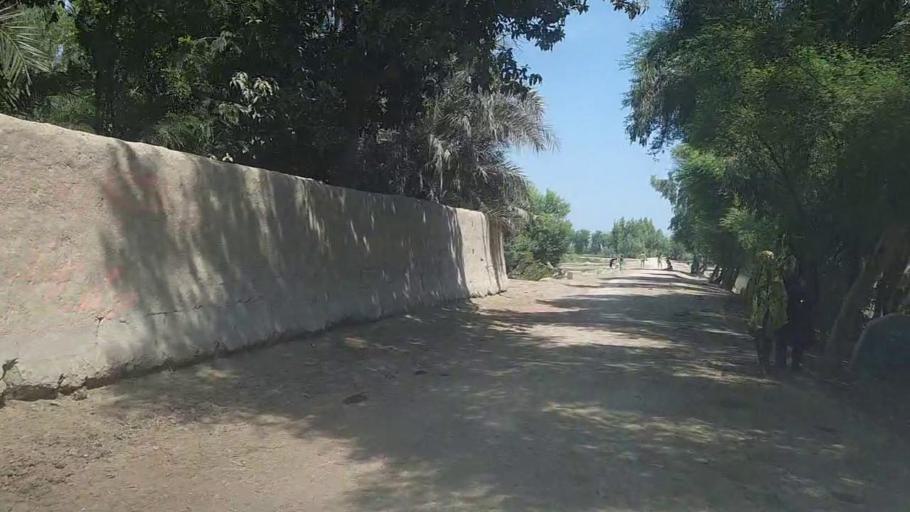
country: PK
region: Sindh
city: Kandhkot
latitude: 28.2687
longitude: 69.2130
